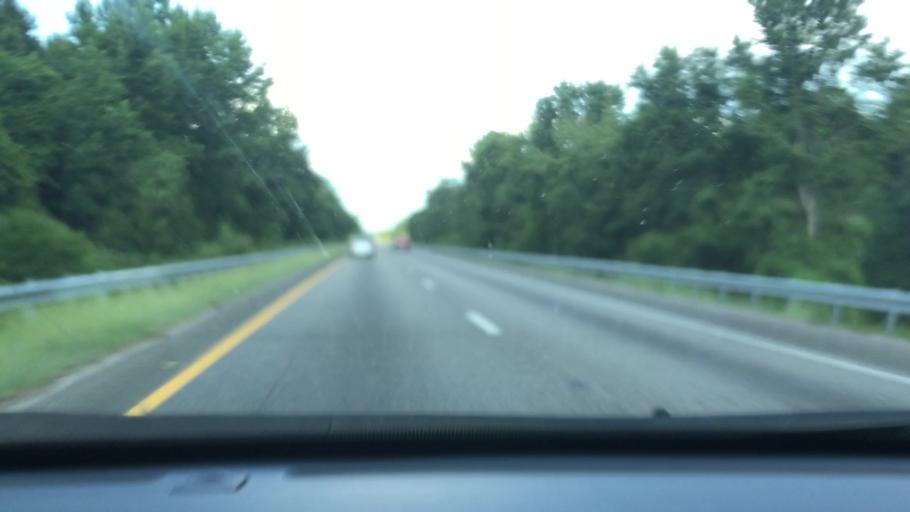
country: US
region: South Carolina
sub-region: Florence County
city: Florence
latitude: 34.2855
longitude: -79.6695
